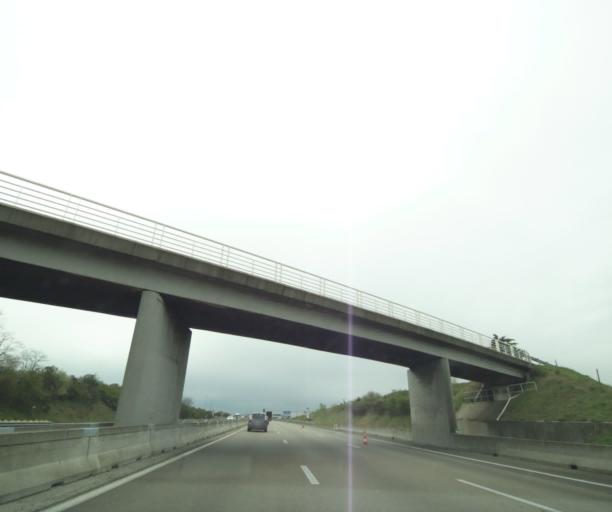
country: FR
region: Rhone-Alpes
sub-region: Departement de la Drome
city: La Roche-de-Glun
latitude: 45.0278
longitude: 4.8750
